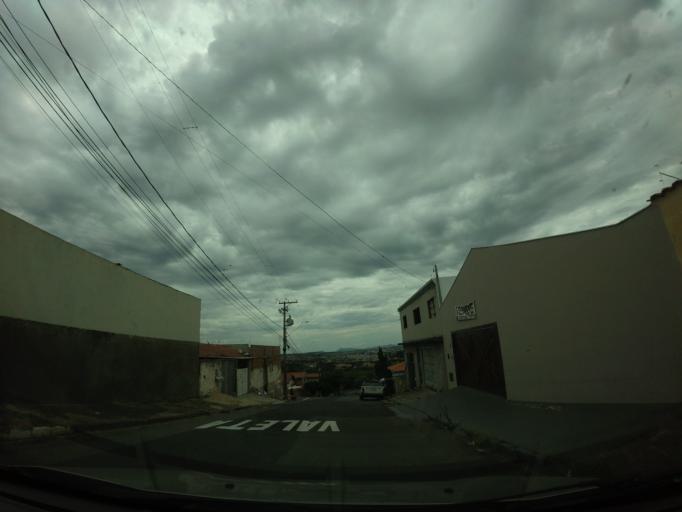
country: BR
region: Sao Paulo
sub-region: Piracicaba
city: Piracicaba
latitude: -22.7582
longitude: -47.6012
